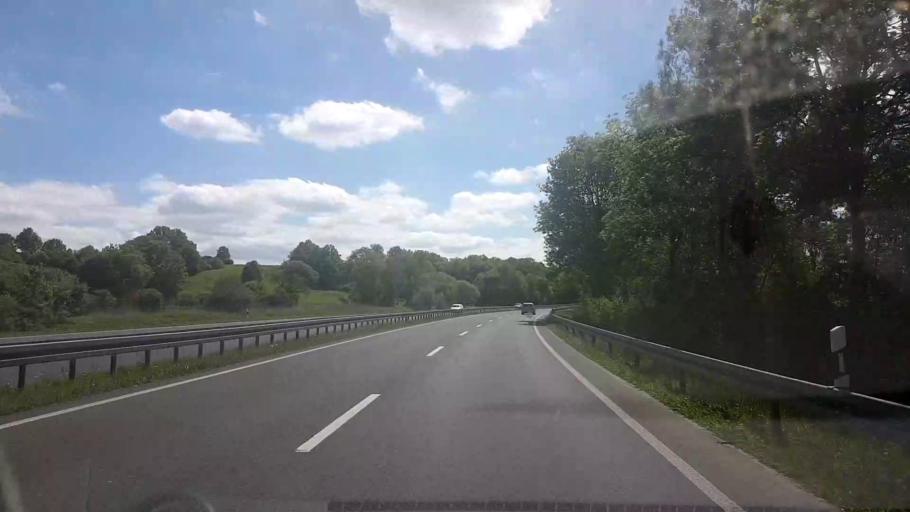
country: DE
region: Bavaria
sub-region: Upper Franconia
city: Niederfullbach
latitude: 50.2146
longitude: 10.9830
